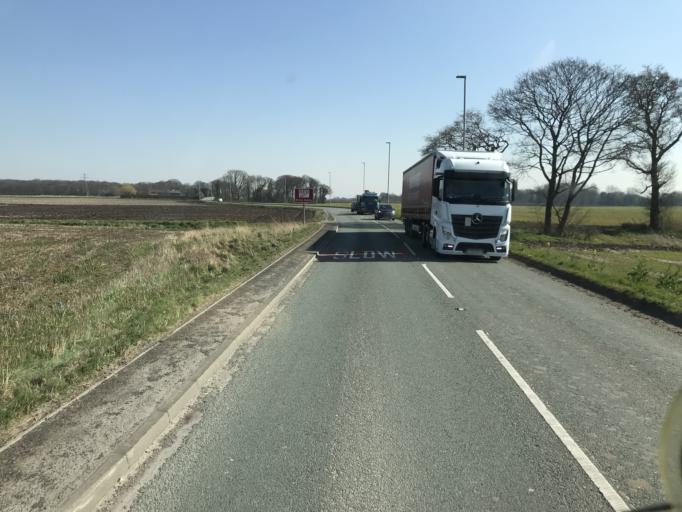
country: GB
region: England
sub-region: Warrington
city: Lymm
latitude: 53.4009
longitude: -2.4932
